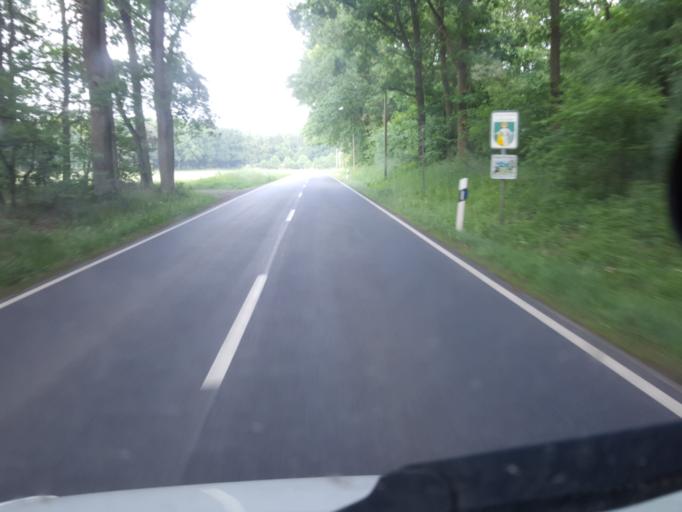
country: DE
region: Lower Saxony
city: Liebenau
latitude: 52.5870
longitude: 9.0768
